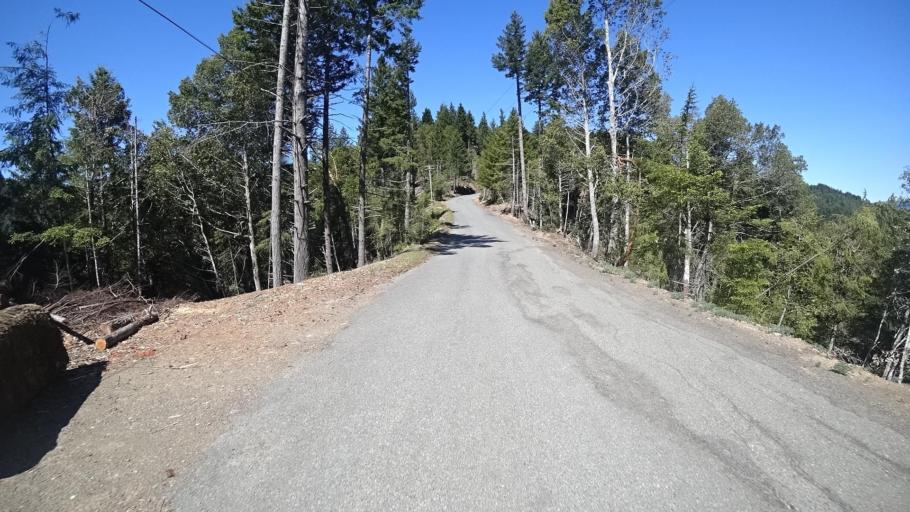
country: US
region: California
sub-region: Humboldt County
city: Redway
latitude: 40.1533
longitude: -124.0683
